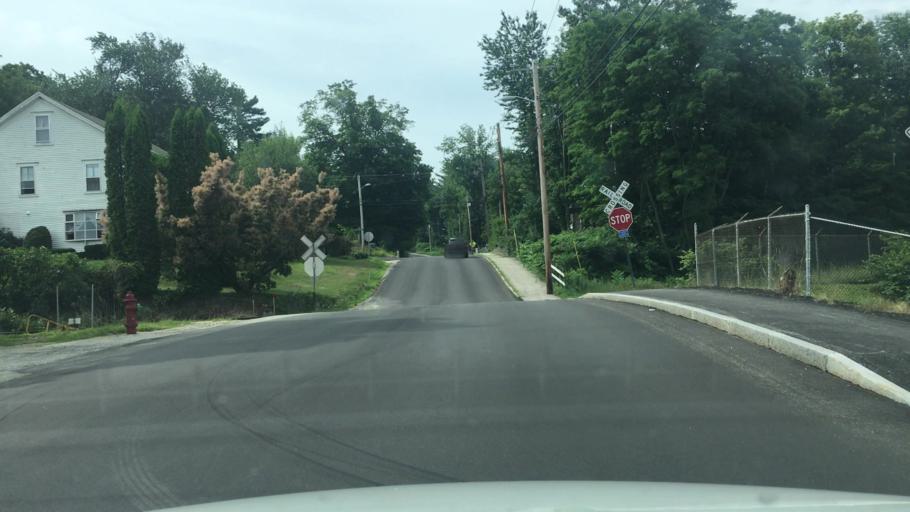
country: US
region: New Hampshire
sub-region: Belknap County
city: Meredith
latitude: 43.6510
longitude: -71.5002
